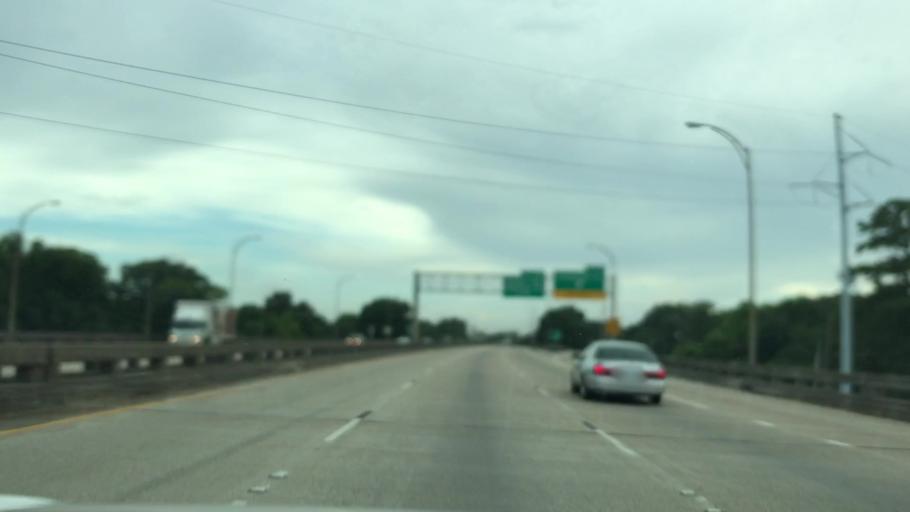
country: US
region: Louisiana
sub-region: East Baton Rouge Parish
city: Baton Rouge
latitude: 30.4950
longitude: -91.1617
